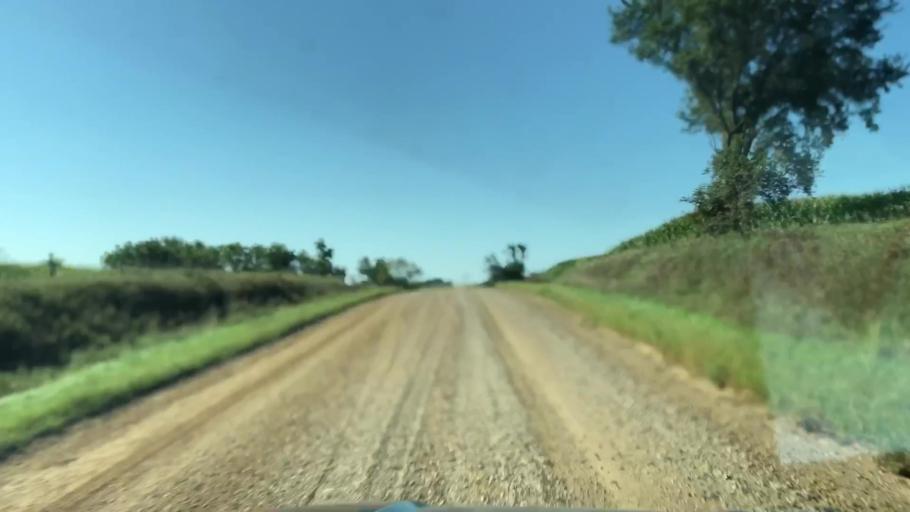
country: US
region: Iowa
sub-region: Woodbury County
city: Sergeant Bluff
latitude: 42.4685
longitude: -96.2525
